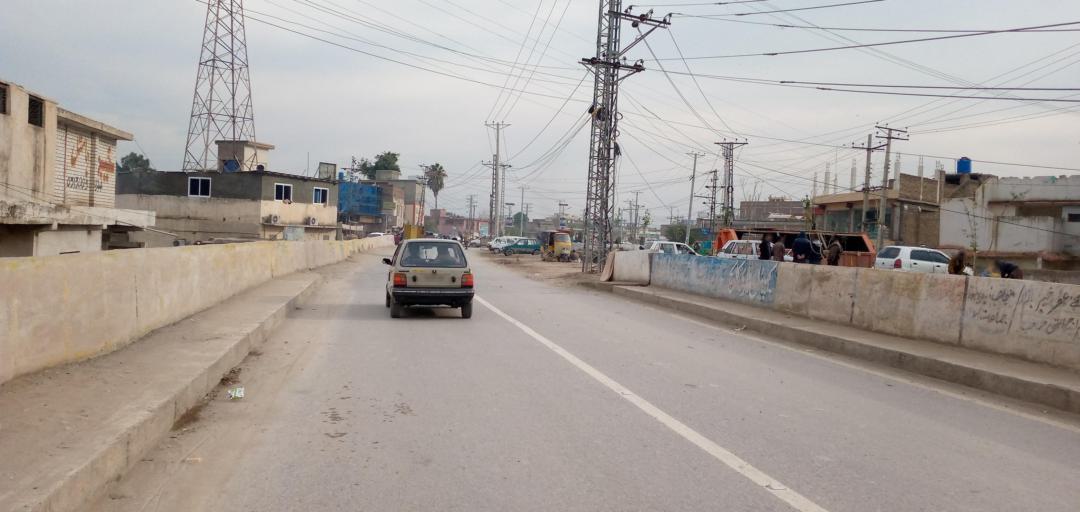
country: PK
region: Khyber Pakhtunkhwa
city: Peshawar
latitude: 34.0037
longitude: 71.4669
